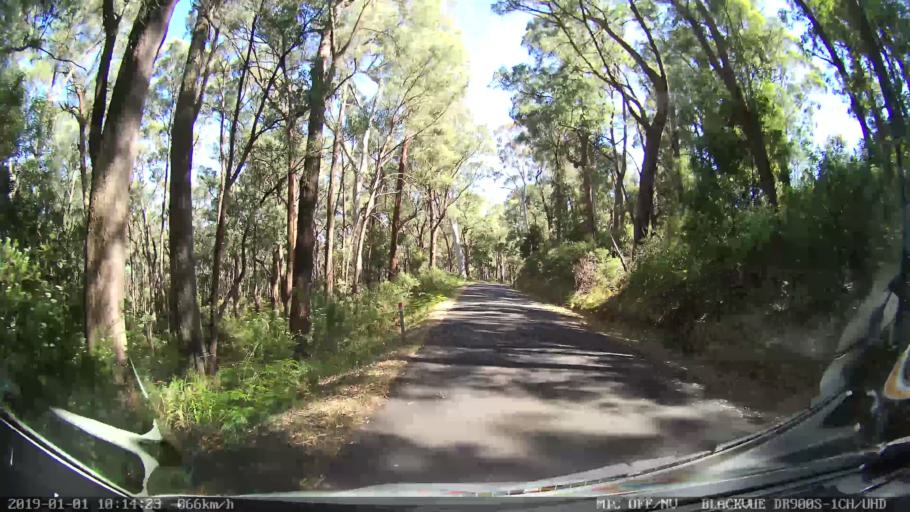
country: AU
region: New South Wales
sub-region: Snowy River
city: Jindabyne
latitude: -36.1127
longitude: 148.1608
